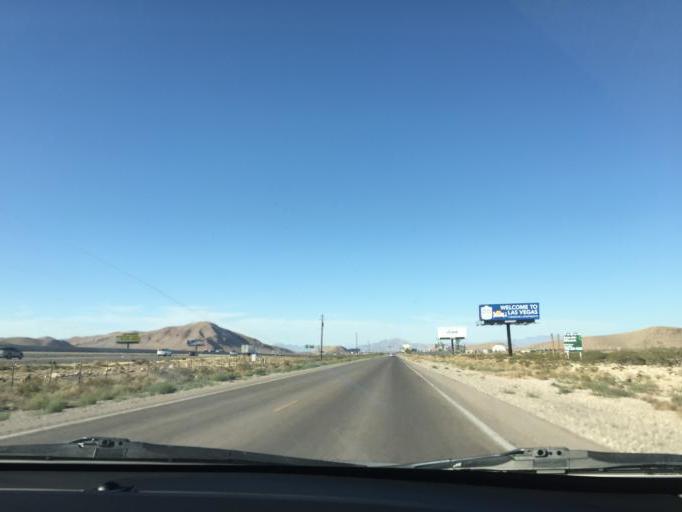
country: US
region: Nevada
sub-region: Clark County
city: Enterprise
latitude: 35.9173
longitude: -115.2016
